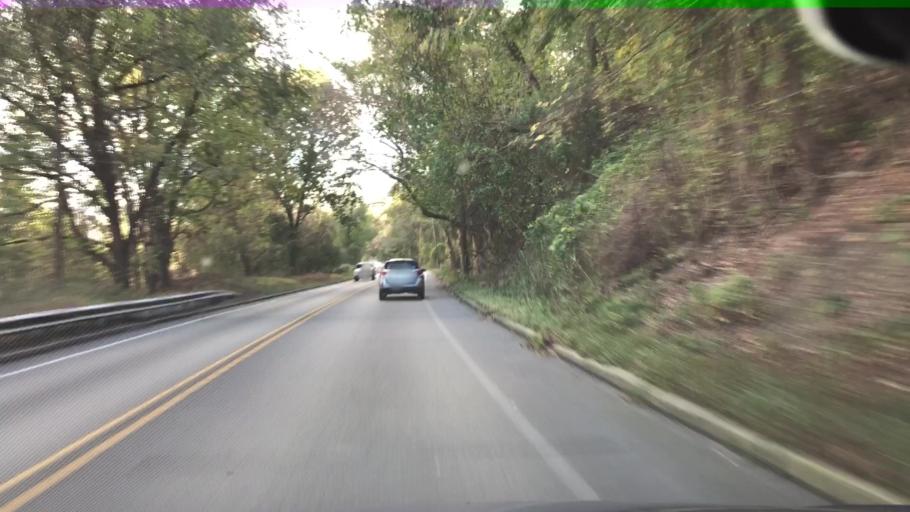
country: US
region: Pennsylvania
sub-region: Allegheny County
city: Aspinwall
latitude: 40.4828
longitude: -79.8968
